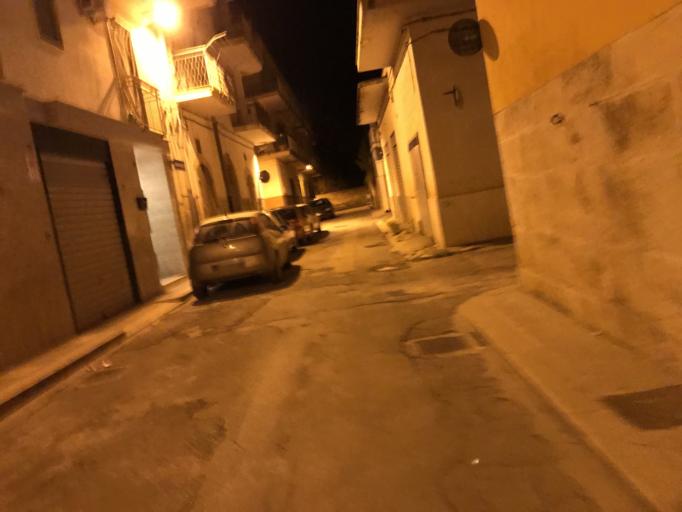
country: IT
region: Apulia
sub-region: Provincia di Bari
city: Corato
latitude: 41.1516
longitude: 16.4066
